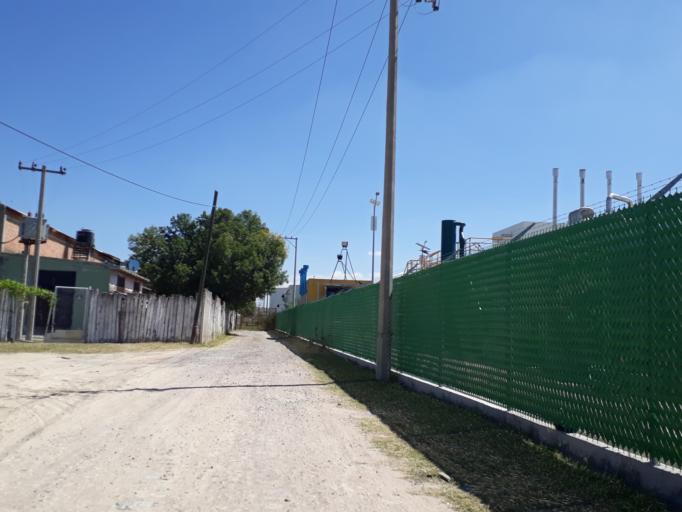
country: MX
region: Aguascalientes
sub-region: Aguascalientes
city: San Sebastian [Fraccionamiento]
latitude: 21.8062
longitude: -102.2901
